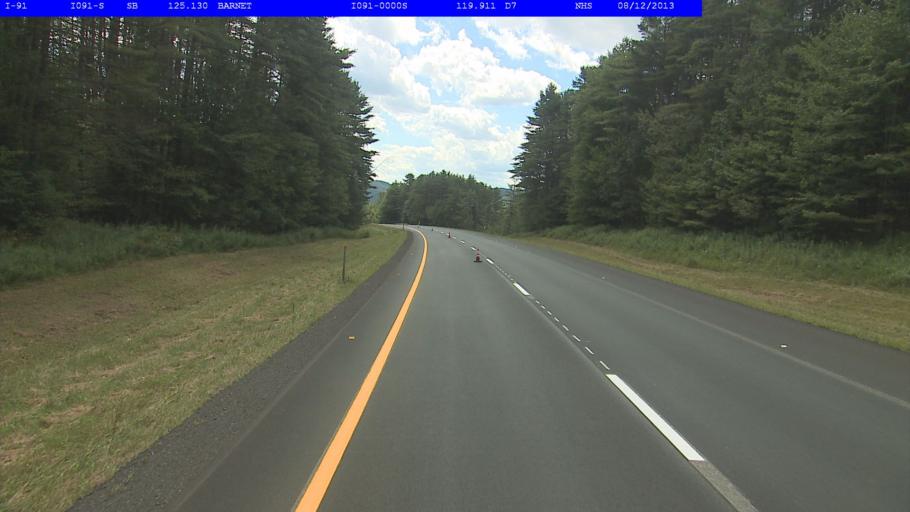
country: US
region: Vermont
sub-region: Caledonia County
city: Saint Johnsbury
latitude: 44.3542
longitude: -72.0356
